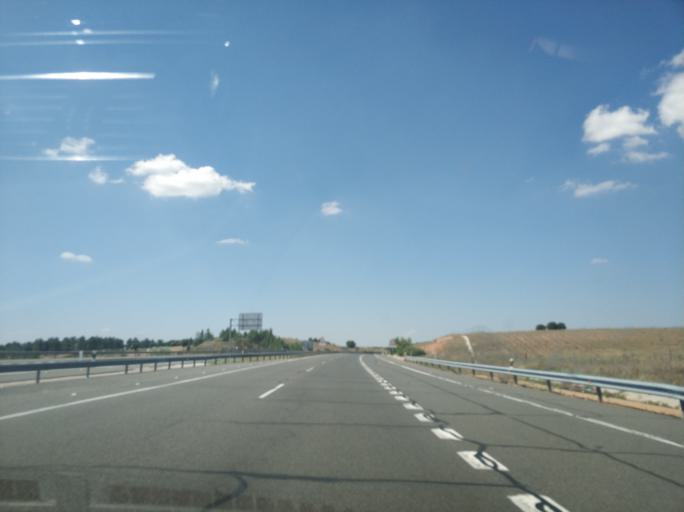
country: ES
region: Castille and Leon
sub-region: Provincia de Zamora
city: Cuelgamures
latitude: 41.2669
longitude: -5.7053
